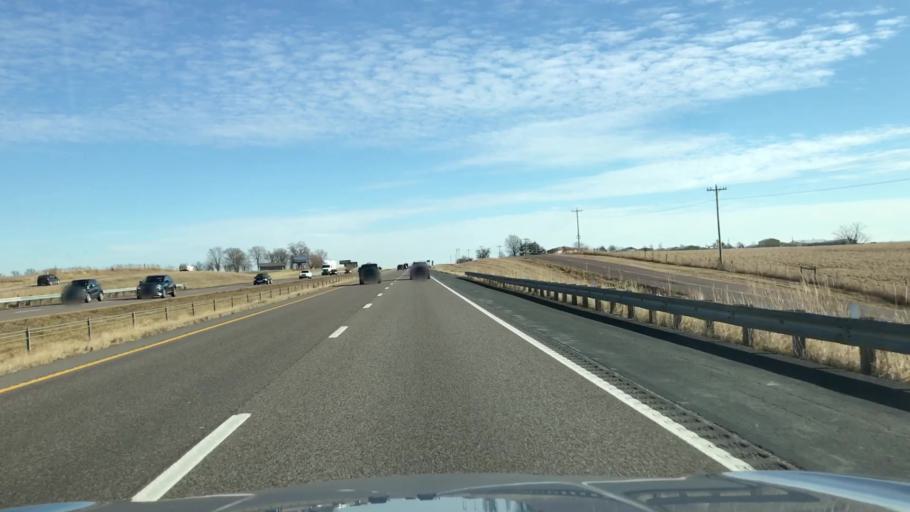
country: US
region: Missouri
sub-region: Callaway County
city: Fulton
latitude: 38.9438
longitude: -91.9079
